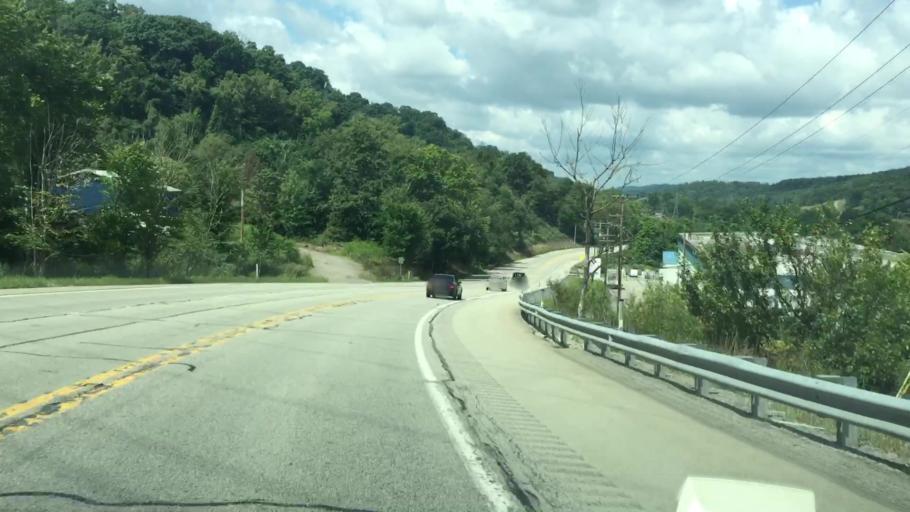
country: US
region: Pennsylvania
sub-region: Allegheny County
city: Oakmont
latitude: 40.5532
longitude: -79.8486
